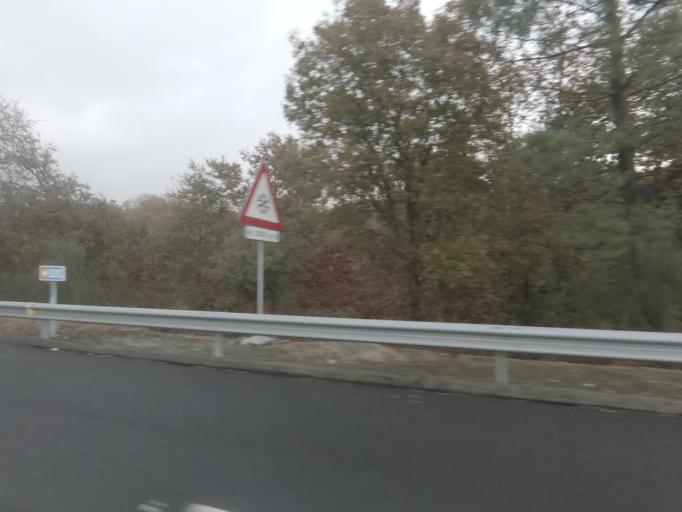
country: ES
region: Galicia
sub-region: Provincia de Pontevedra
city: Vigo
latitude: 42.2022
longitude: -8.6681
